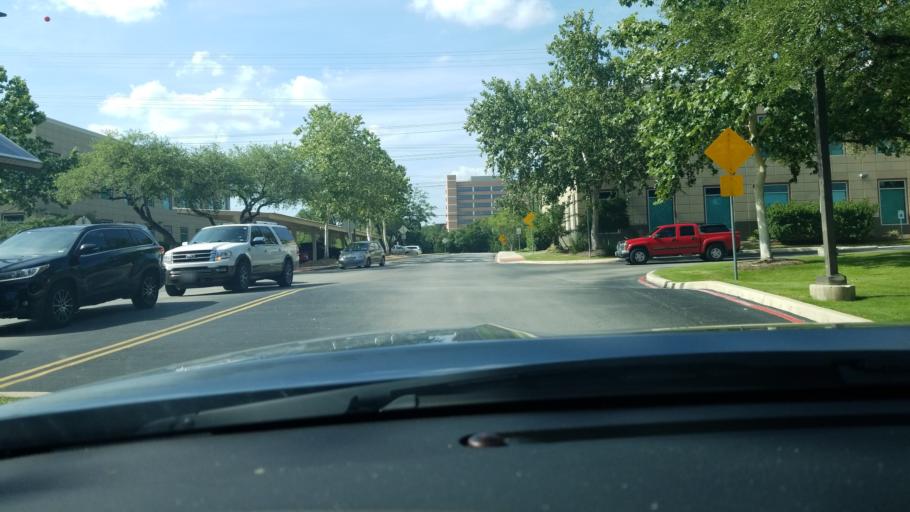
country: US
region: Texas
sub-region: Bexar County
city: Hollywood Park
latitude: 29.6165
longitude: -98.4911
